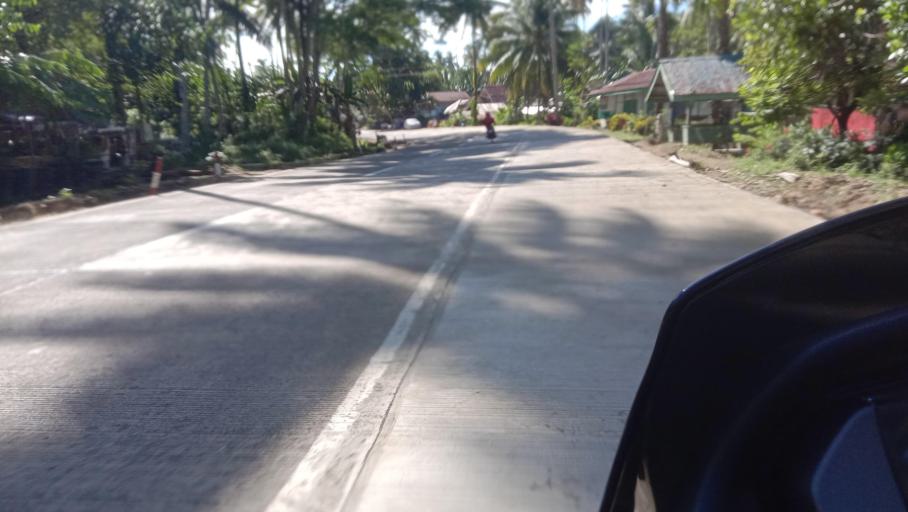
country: PH
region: Caraga
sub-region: Province of Surigao del Sur
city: Amaga
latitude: 8.5365
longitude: 126.0905
